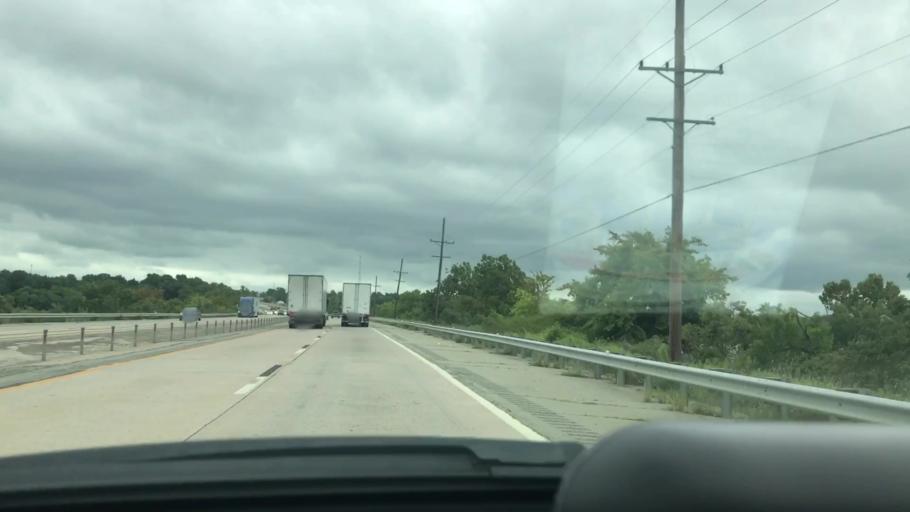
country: US
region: Oklahoma
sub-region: McIntosh County
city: Eufaula
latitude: 35.3471
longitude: -95.5805
